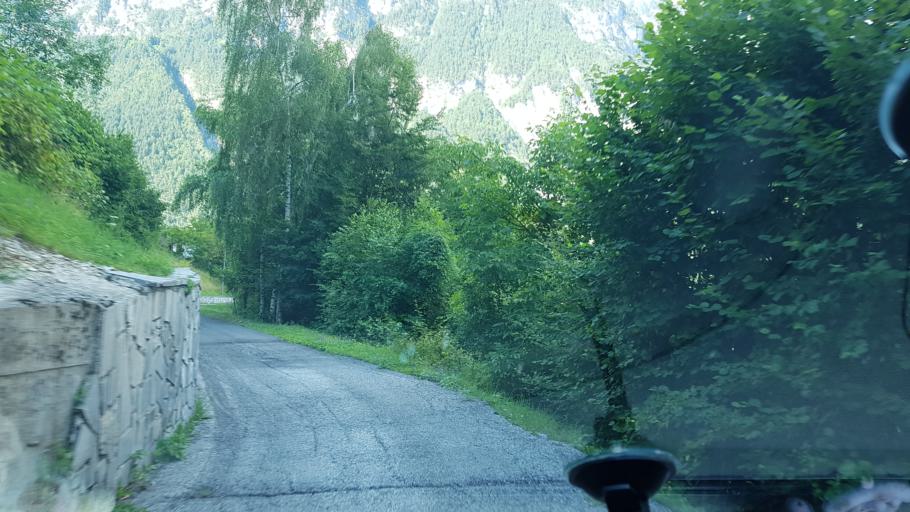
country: IT
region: Friuli Venezia Giulia
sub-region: Provincia di Udine
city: Dogna
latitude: 46.4480
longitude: 13.3108
